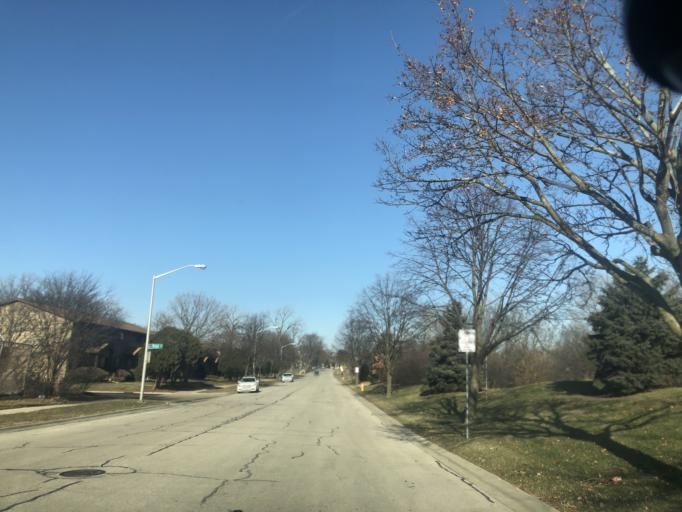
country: US
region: Illinois
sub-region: DuPage County
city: Addison
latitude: 41.9251
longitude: -87.9912
